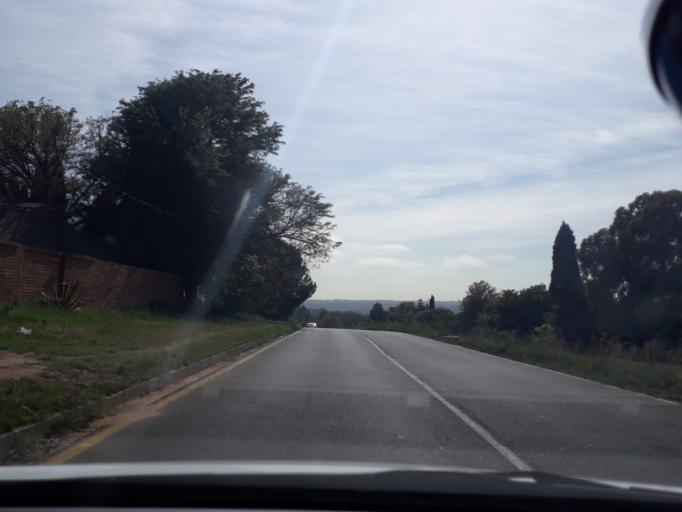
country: ZA
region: Gauteng
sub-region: City of Johannesburg Metropolitan Municipality
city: Roodepoort
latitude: -26.1180
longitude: 27.9382
